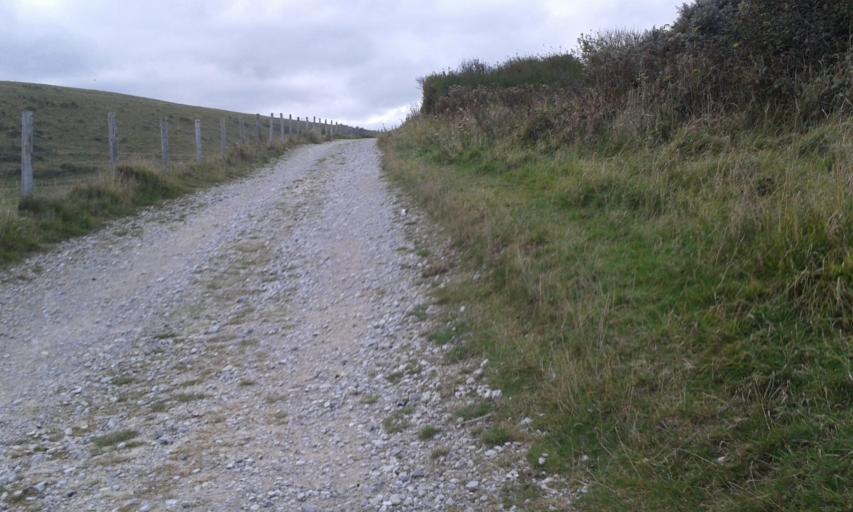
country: FR
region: Nord-Pas-de-Calais
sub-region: Departement du Pas-de-Calais
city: Sangatte
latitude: 50.9356
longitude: 1.7332
